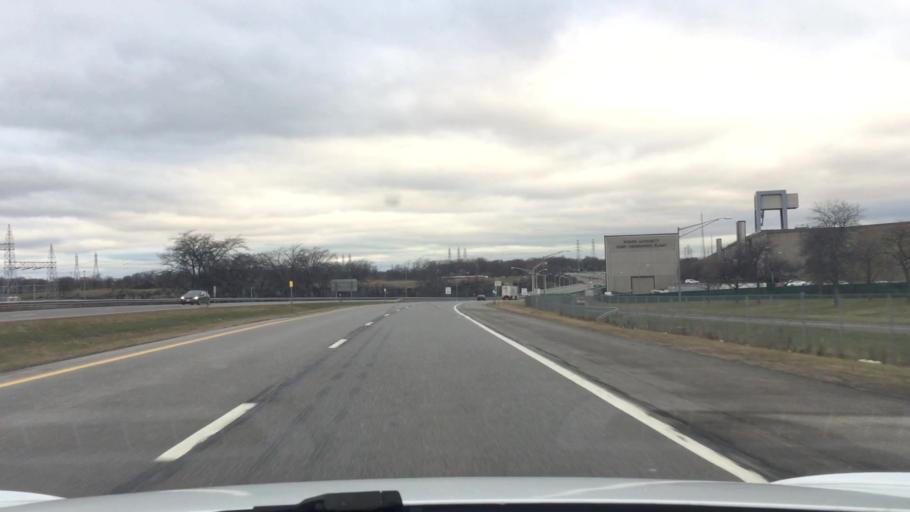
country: US
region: New York
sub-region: Niagara County
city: Lewiston
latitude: 43.1381
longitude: -79.0216
